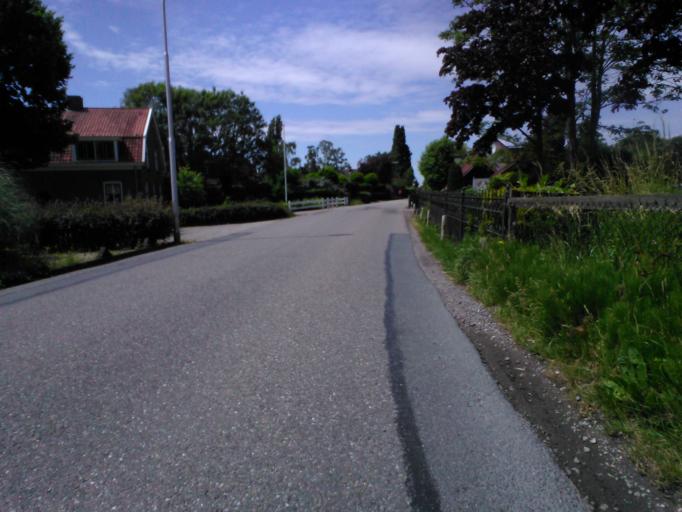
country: NL
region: South Holland
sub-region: Gemeente Alblasserdam
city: Alblasserdam
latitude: 51.8583
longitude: 4.6854
